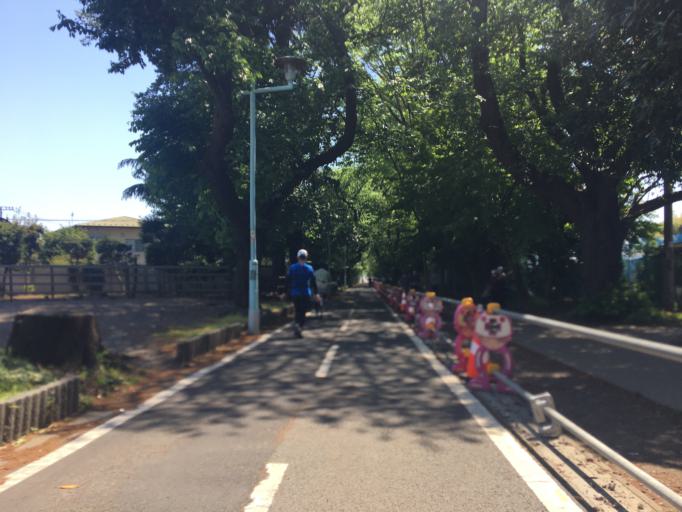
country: JP
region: Tokyo
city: Tanashicho
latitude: 35.7246
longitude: 139.5152
